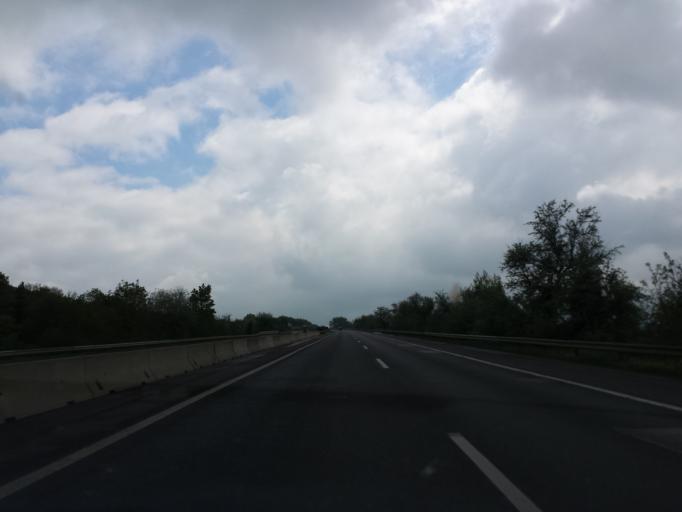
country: HU
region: Komarom-Esztergom
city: Tatabanya
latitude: 47.5830
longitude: 18.4077
